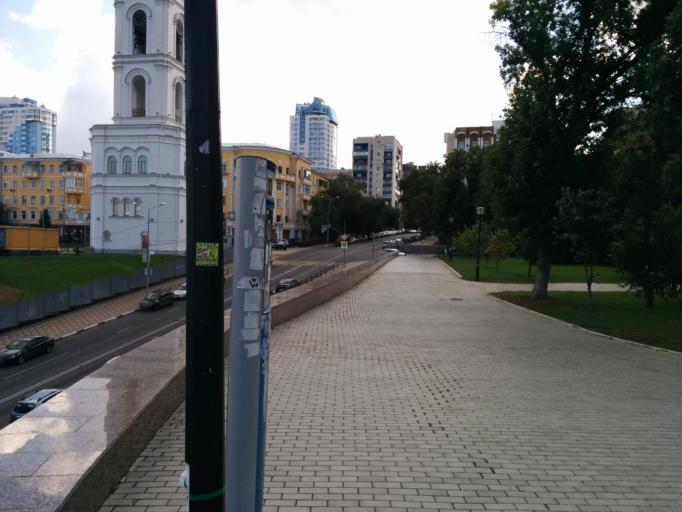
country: RU
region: Samara
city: Samara
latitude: 53.1989
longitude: 50.0974
